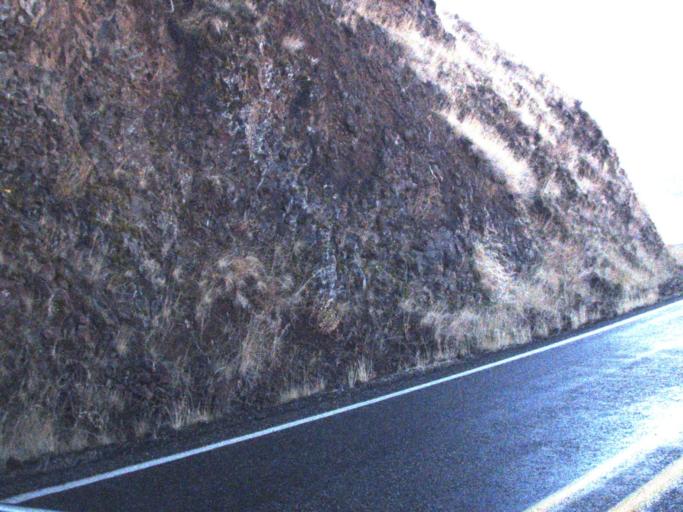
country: US
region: Washington
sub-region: Asotin County
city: Asotin
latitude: 46.0696
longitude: -117.2218
